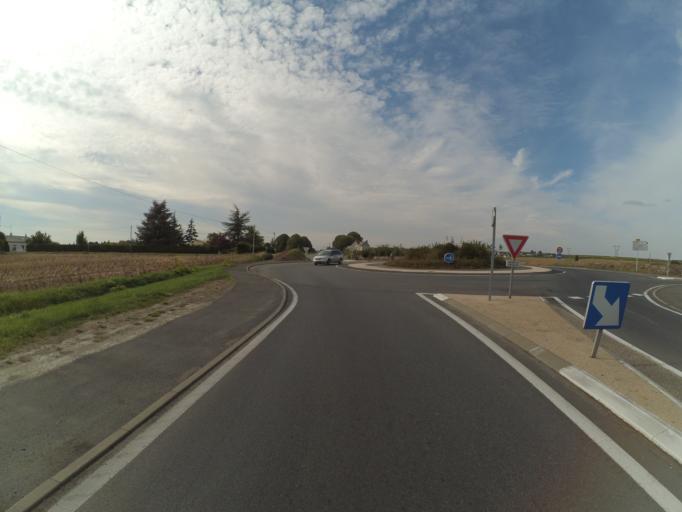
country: FR
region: Pays de la Loire
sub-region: Departement de Maine-et-Loire
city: Distre
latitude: 47.2139
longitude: -0.1759
